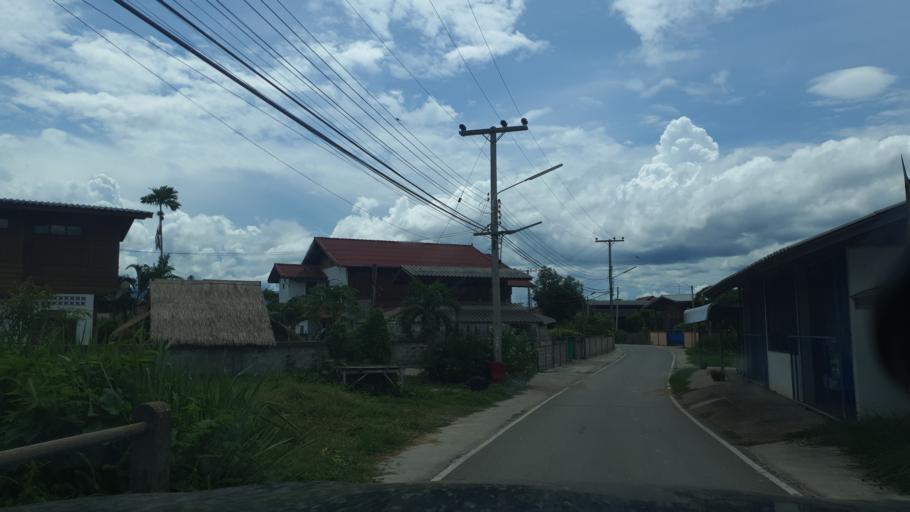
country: TH
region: Lampang
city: Sop Prap
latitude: 17.8830
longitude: 99.3823
